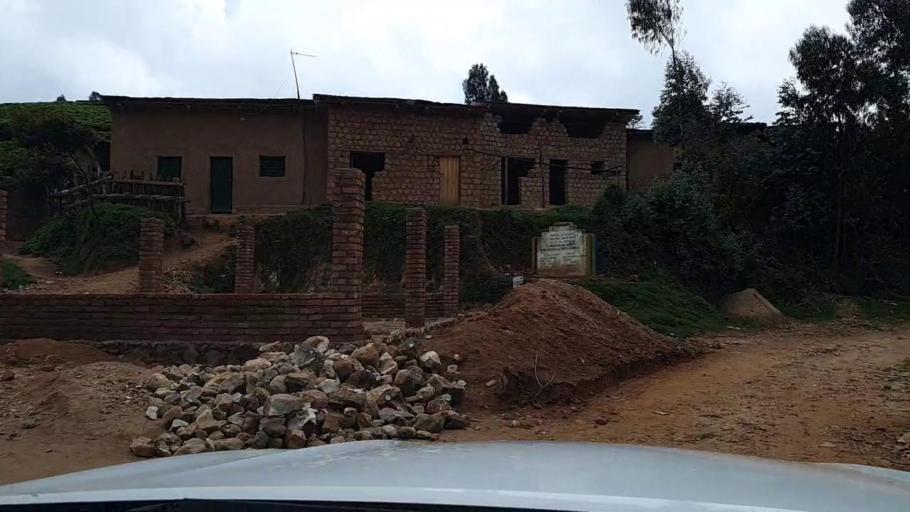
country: RW
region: Western Province
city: Kibuye
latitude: -2.2886
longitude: 29.3678
